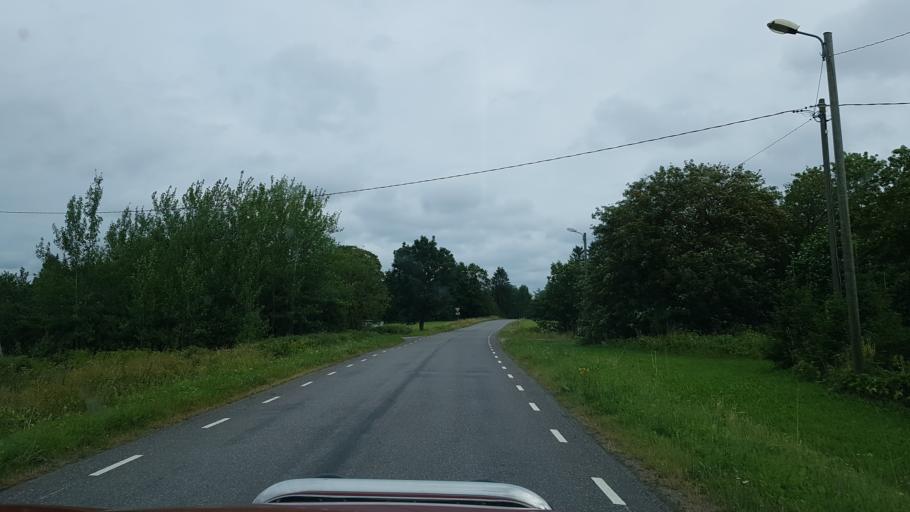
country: EE
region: Ida-Virumaa
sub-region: Kivioli linn
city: Kivioli
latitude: 59.4112
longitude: 27.0027
